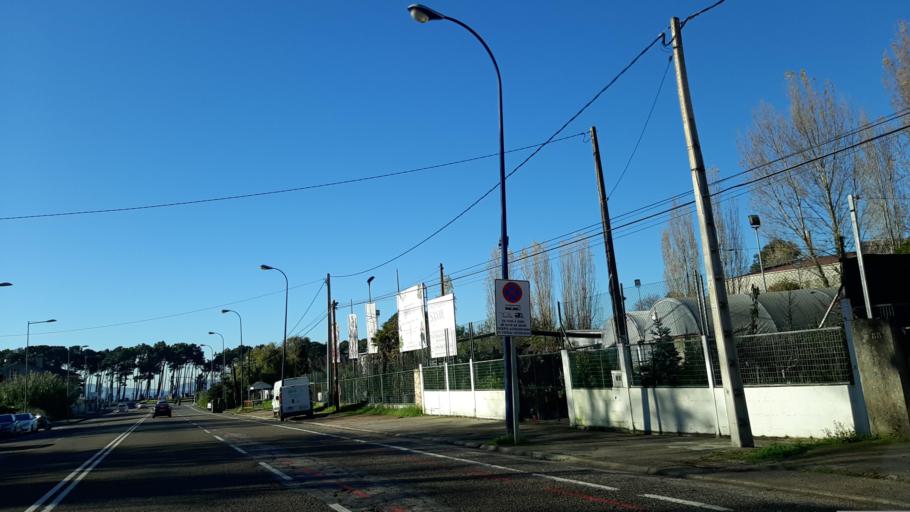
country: ES
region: Galicia
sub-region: Provincia de Pontevedra
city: Vigo
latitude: 42.2110
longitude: -8.7712
